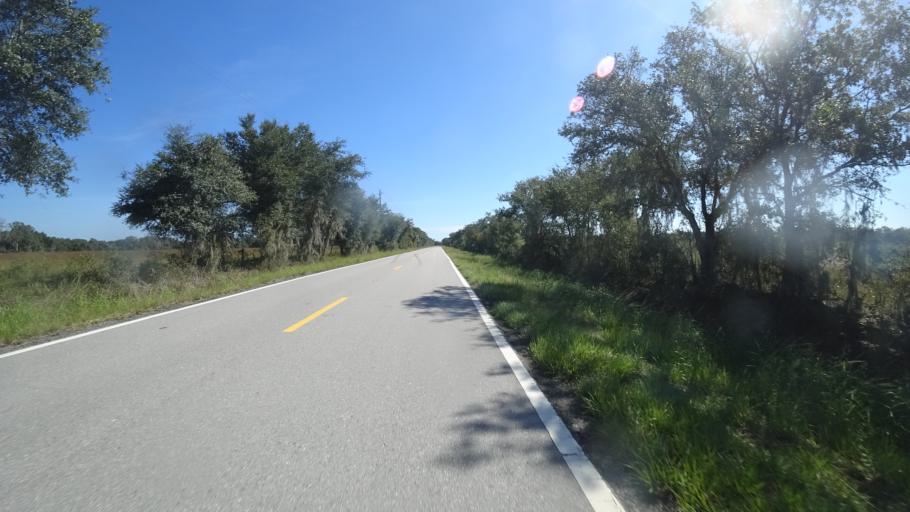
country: US
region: Florida
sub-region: Sarasota County
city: Lake Sarasota
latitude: 27.2904
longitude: -82.2411
